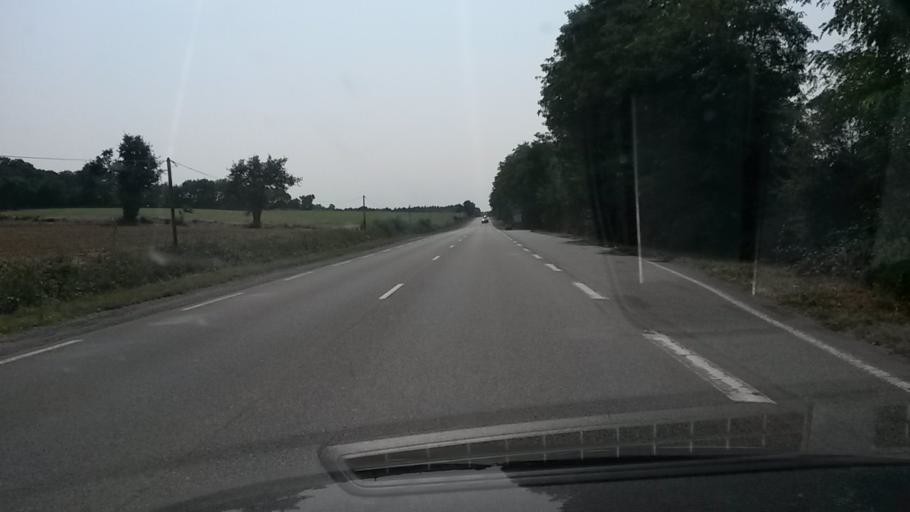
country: FR
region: Pays de la Loire
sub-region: Departement de la Mayenne
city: Chateau-Gontier
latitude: 47.8638
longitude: -0.6900
